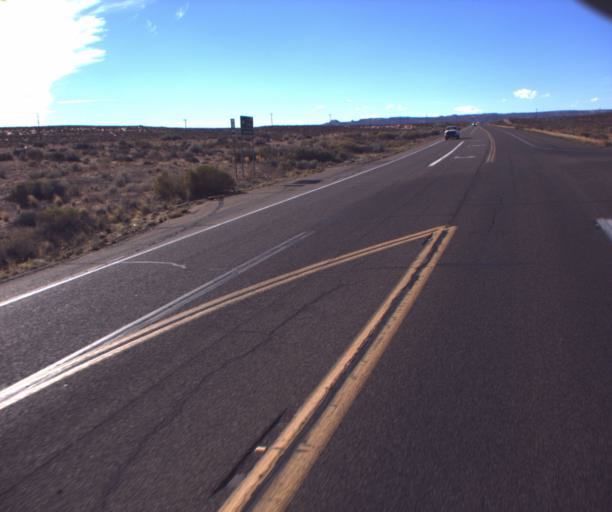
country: US
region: Arizona
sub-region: Coconino County
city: Page
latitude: 36.9802
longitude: -111.5266
